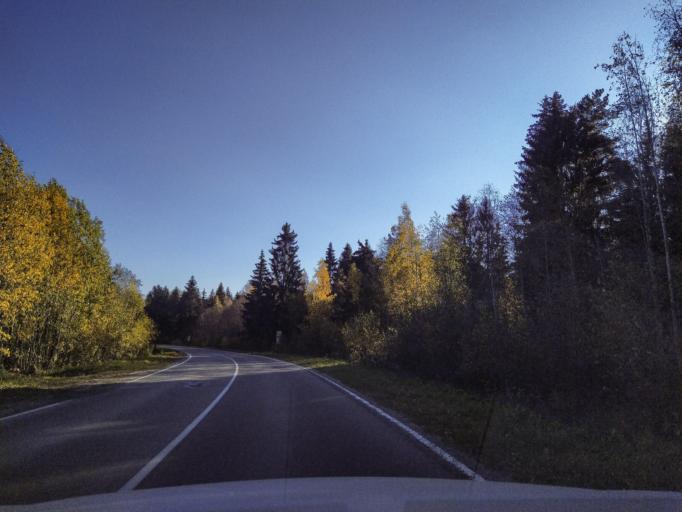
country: RU
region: Leningrad
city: Siverskiy
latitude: 59.3089
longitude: 30.0292
